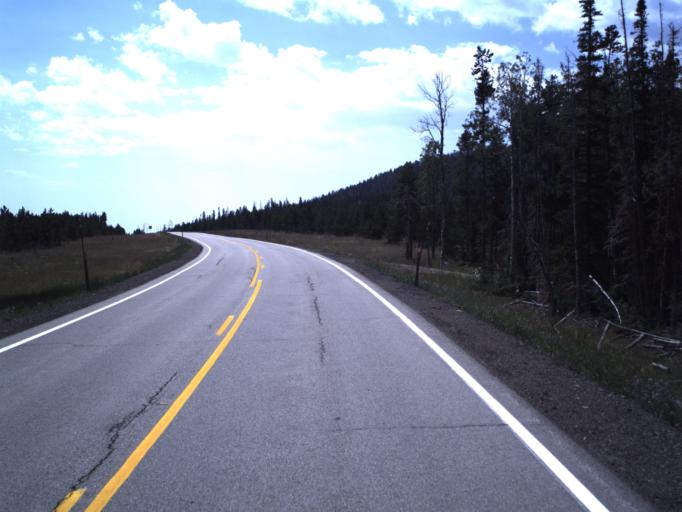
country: US
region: Utah
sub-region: Uintah County
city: Maeser
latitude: 40.7486
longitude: -109.4723
